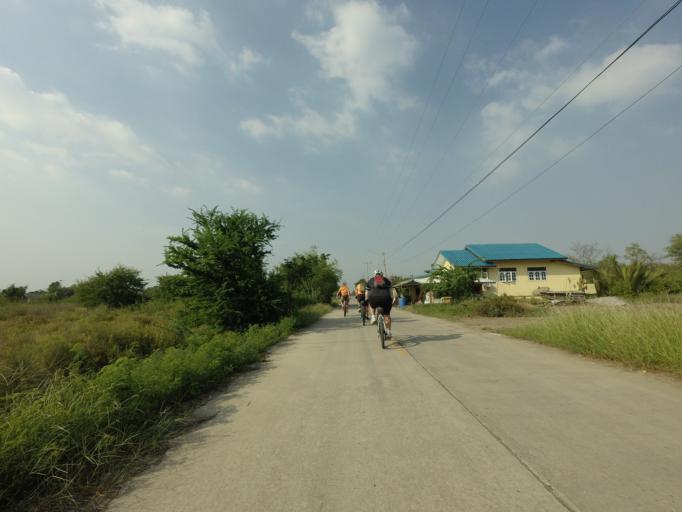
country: TH
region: Samut Sakhon
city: Samut Sakhon
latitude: 13.5025
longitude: 100.3278
